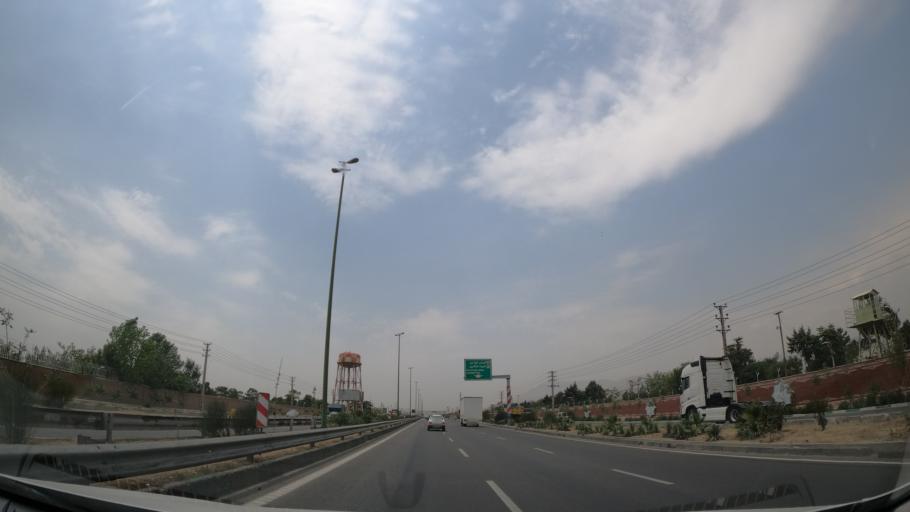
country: IR
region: Tehran
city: Shahr-e Qods
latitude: 35.6935
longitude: 51.2083
